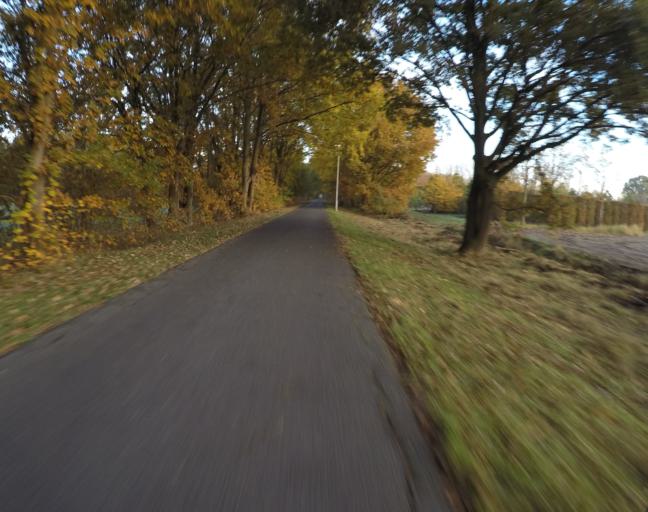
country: BE
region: Flanders
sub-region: Provincie Antwerpen
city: Hulshout
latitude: 51.0525
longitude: 4.8250
